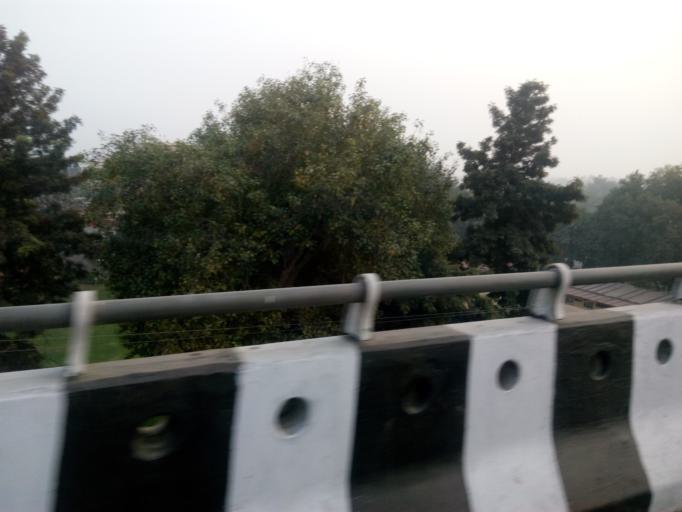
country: IN
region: NCT
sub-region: Central Delhi
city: Karol Bagh
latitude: 28.5727
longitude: 77.1382
